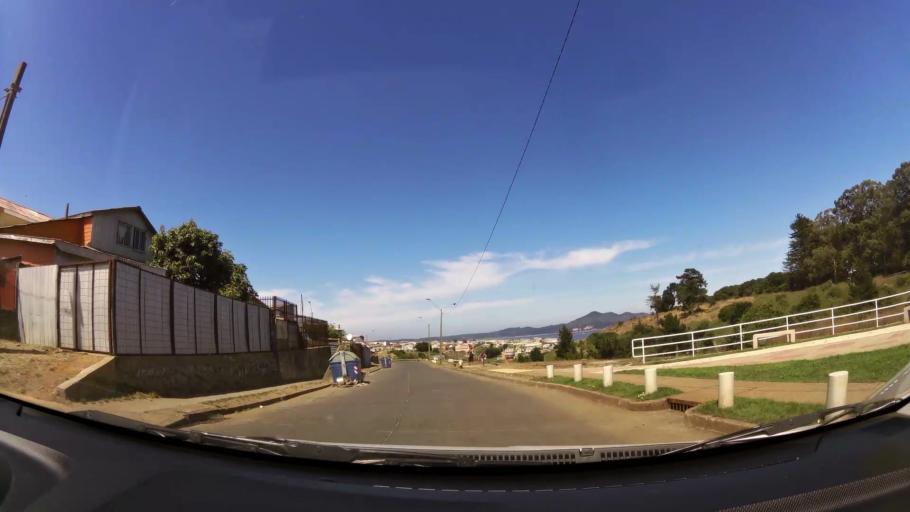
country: CL
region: Biobio
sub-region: Provincia de Concepcion
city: Talcahuano
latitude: -36.7146
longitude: -73.1409
